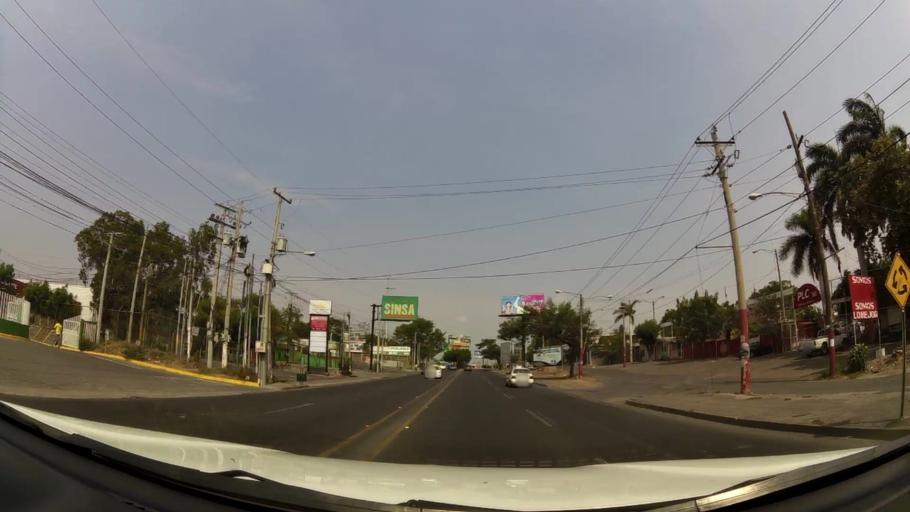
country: NI
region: Managua
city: Managua
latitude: 12.1252
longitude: -86.2810
